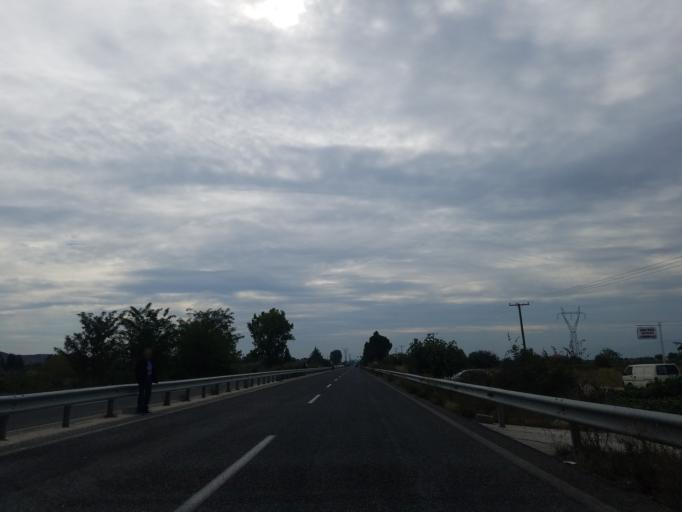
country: GR
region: Thessaly
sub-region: Trikala
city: Vasiliki
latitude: 39.6386
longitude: 21.6956
